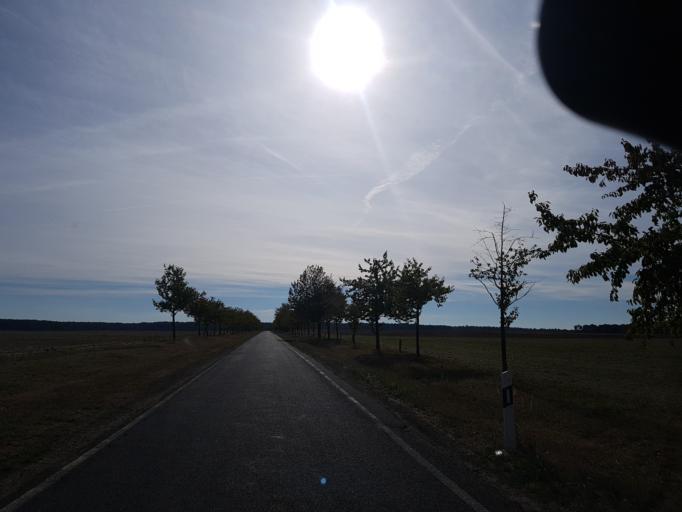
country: DE
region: Brandenburg
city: Ihlow
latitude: 51.8041
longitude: 13.3065
